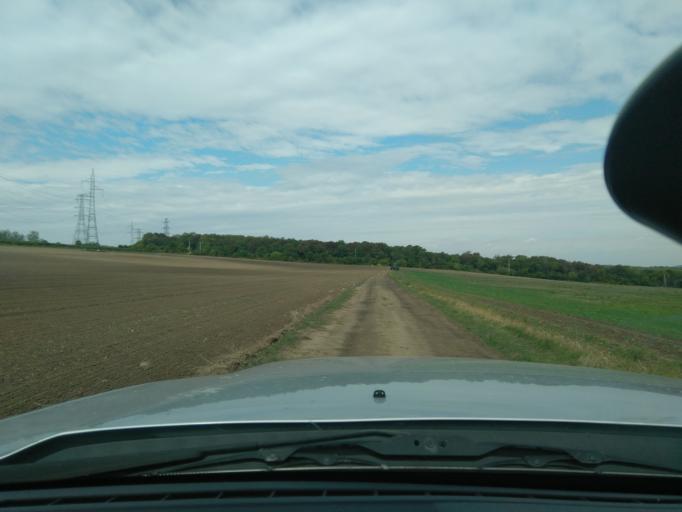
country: HU
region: Fejer
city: Val
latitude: 47.3760
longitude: 18.6929
